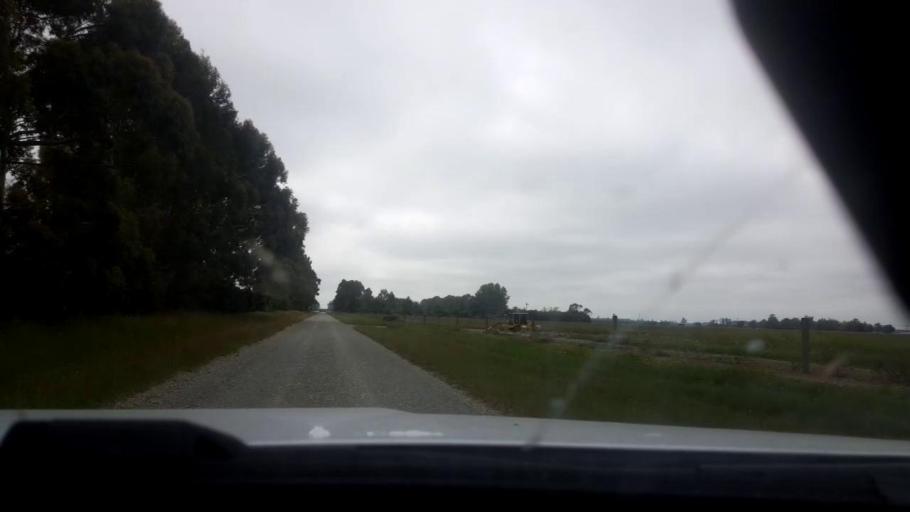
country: NZ
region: Canterbury
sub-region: Timaru District
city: Pleasant Point
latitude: -44.2878
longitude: 171.2083
